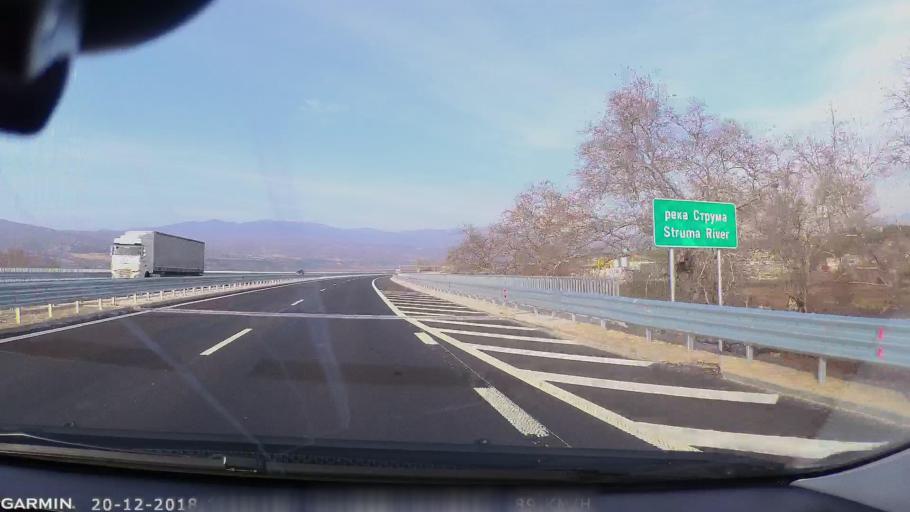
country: BG
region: Blagoevgrad
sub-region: Obshtina Strumyani
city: Strumyani
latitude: 41.6290
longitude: 23.2025
